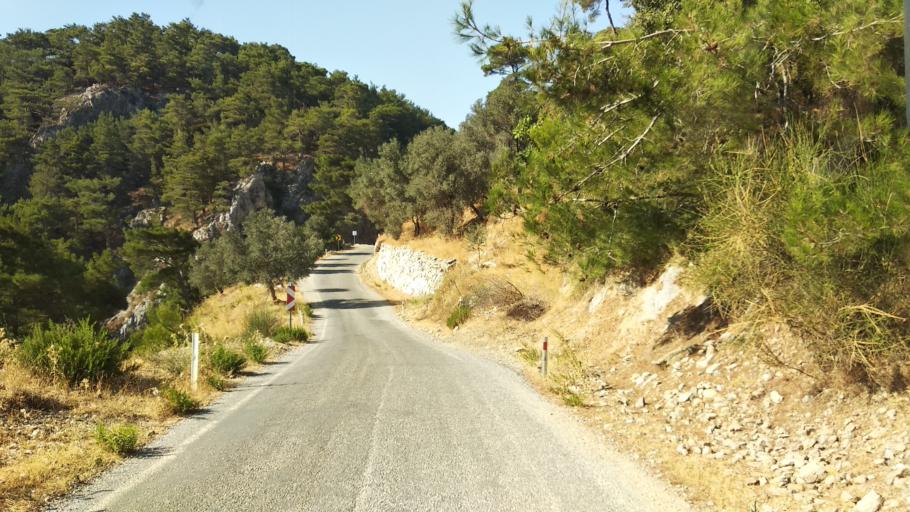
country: TR
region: Izmir
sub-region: Seferihisar
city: Seferhisar
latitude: 38.3200
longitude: 26.9573
